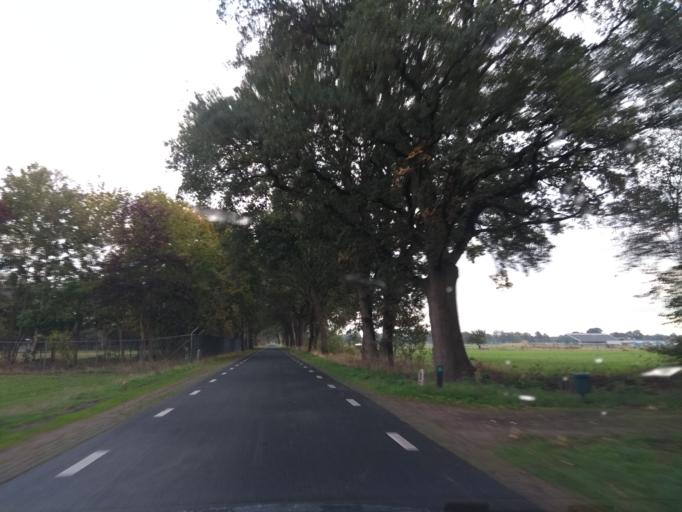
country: NL
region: Gelderland
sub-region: Gemeente Bronckhorst
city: Zelhem
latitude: 52.0297
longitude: 6.3527
